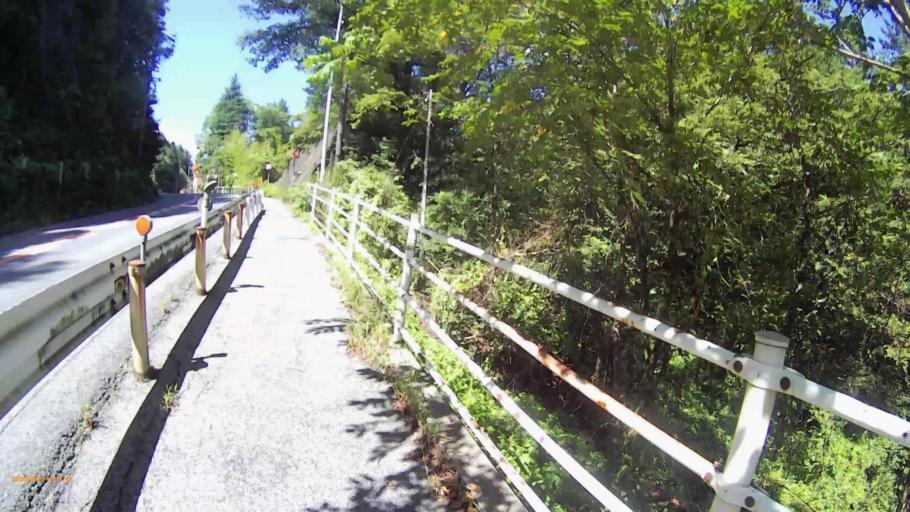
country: JP
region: Nagano
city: Iida
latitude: 35.6841
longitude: 137.6597
